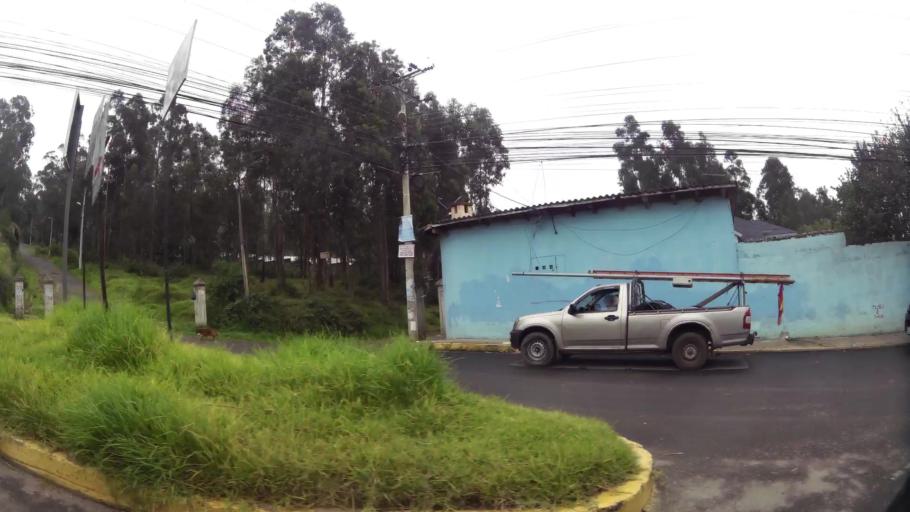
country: EC
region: Pichincha
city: Quito
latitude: -0.2637
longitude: -78.4764
